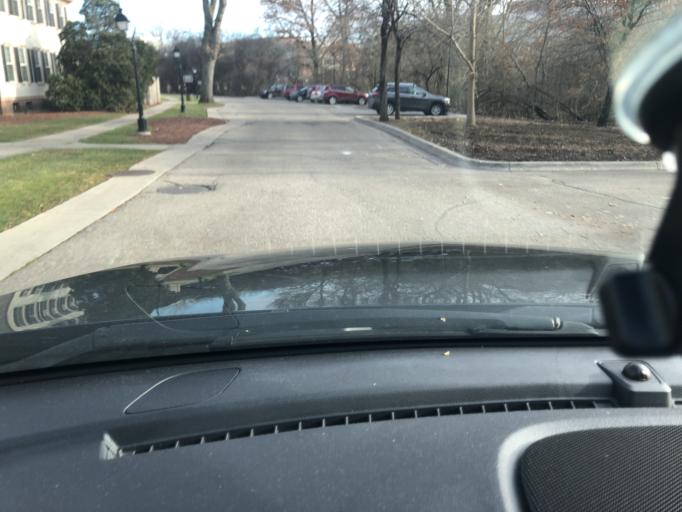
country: US
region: Michigan
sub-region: Wayne County
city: Allen Park
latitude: 42.2959
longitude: -83.2288
